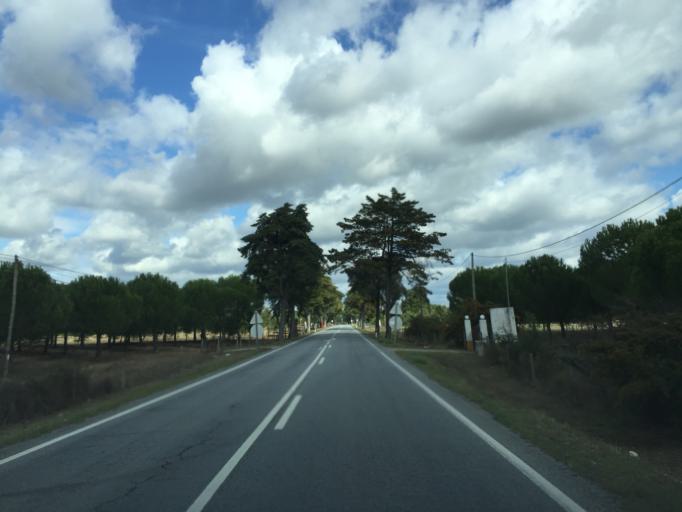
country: PT
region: Portalegre
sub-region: Ponte de Sor
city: Santo Andre
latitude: 39.0949
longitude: -8.1507
